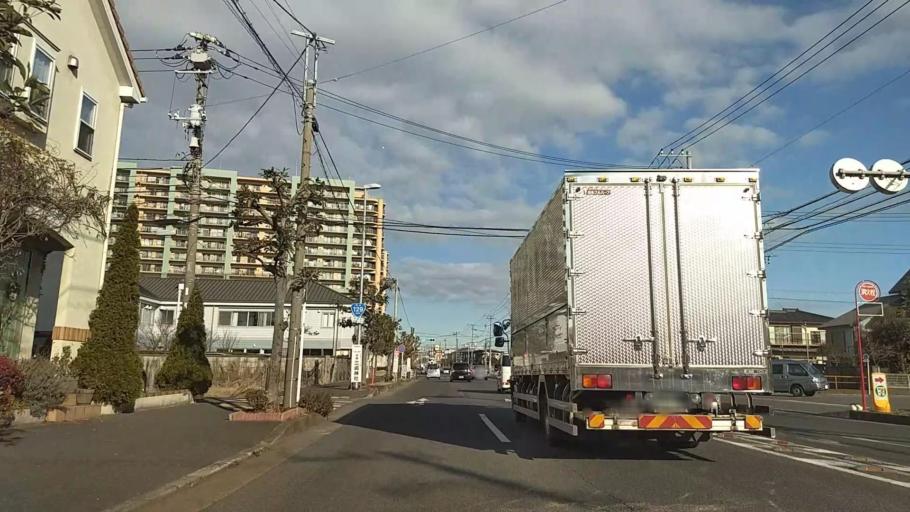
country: JP
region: Kanagawa
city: Hiratsuka
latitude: 35.3246
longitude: 139.3605
